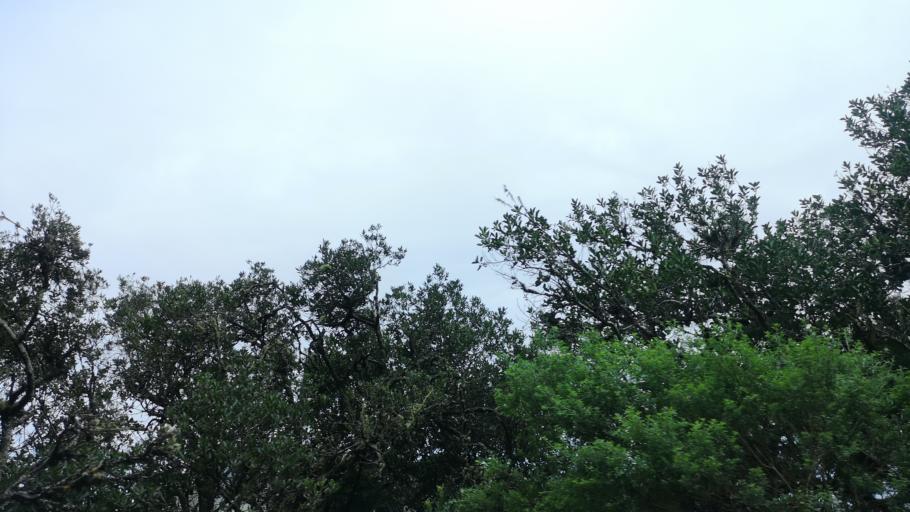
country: ES
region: Canary Islands
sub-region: Provincia de Santa Cruz de Tenerife
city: Vallehermosa
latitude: 28.1621
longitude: -17.2953
